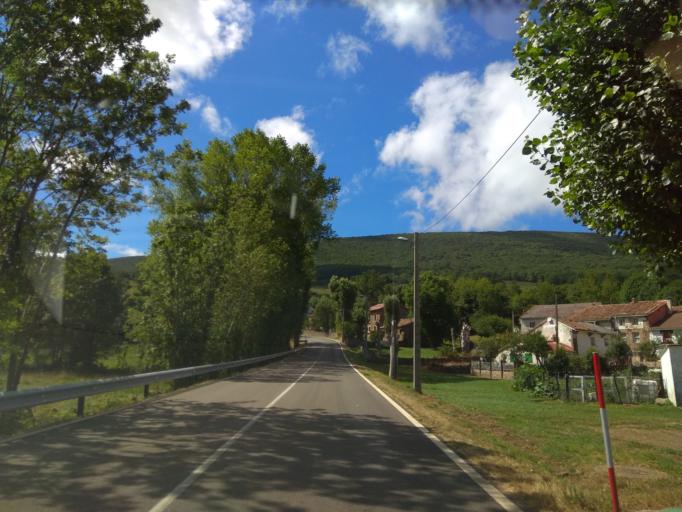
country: ES
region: Cantabria
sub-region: Provincia de Cantabria
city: Villaescusa
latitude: 42.9625
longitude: -4.1659
